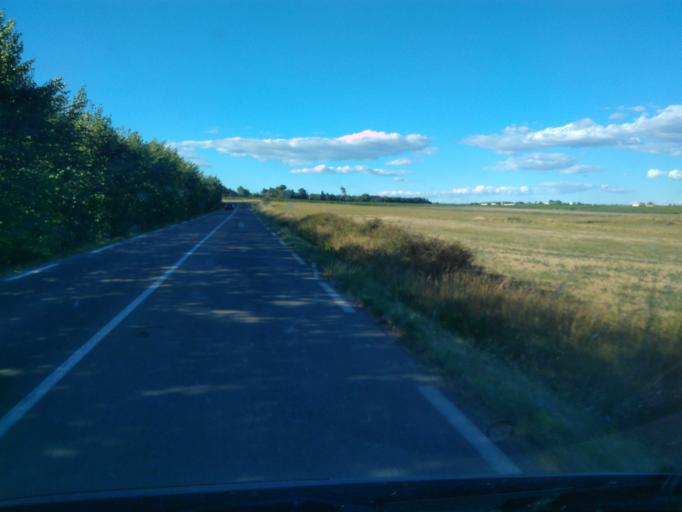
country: FR
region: Languedoc-Roussillon
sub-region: Departement du Gard
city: Vauvert
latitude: 43.6587
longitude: 4.2849
